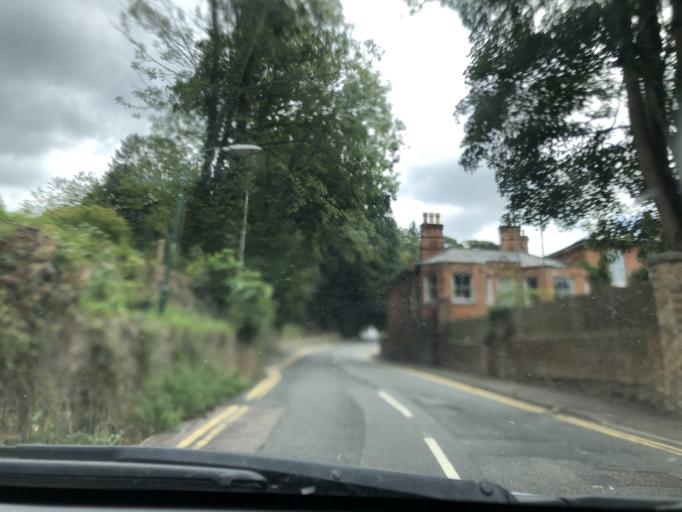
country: GB
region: England
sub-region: Kent
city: Westerham
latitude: 51.2665
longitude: 0.0768
